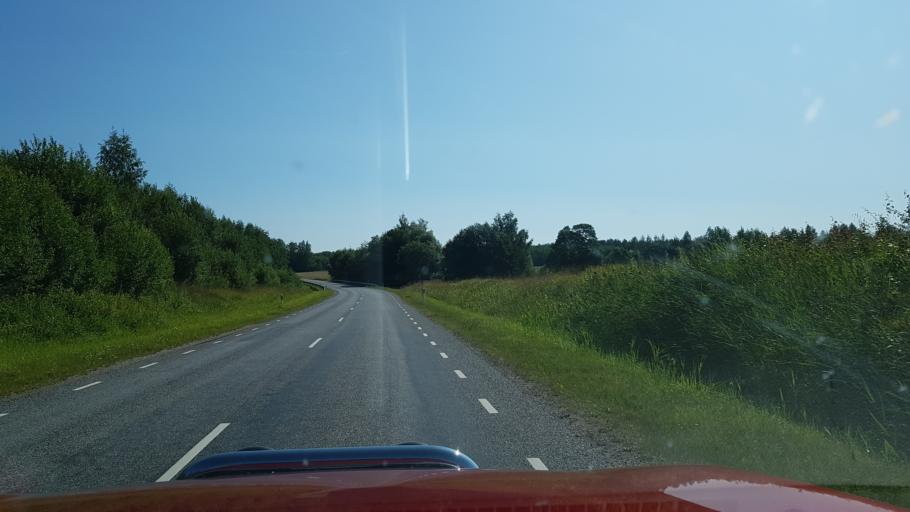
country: EE
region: Vorumaa
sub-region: Voru linn
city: Voru
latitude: 57.9745
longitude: 26.8444
